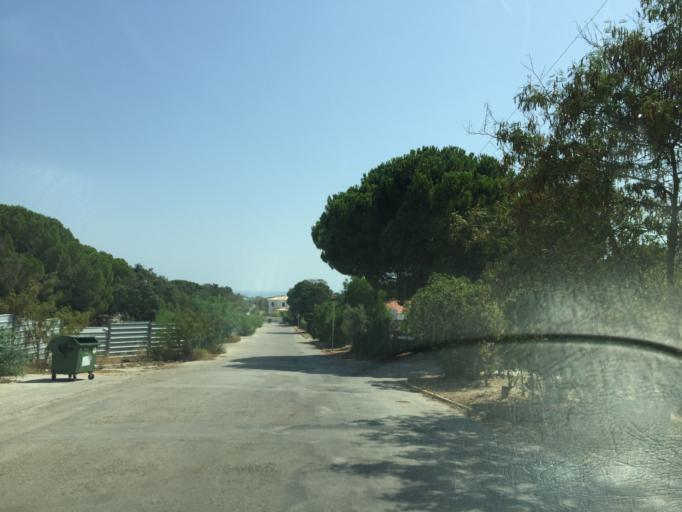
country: PT
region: Faro
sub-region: Albufeira
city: Ferreiras
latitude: 37.1077
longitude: -8.2049
